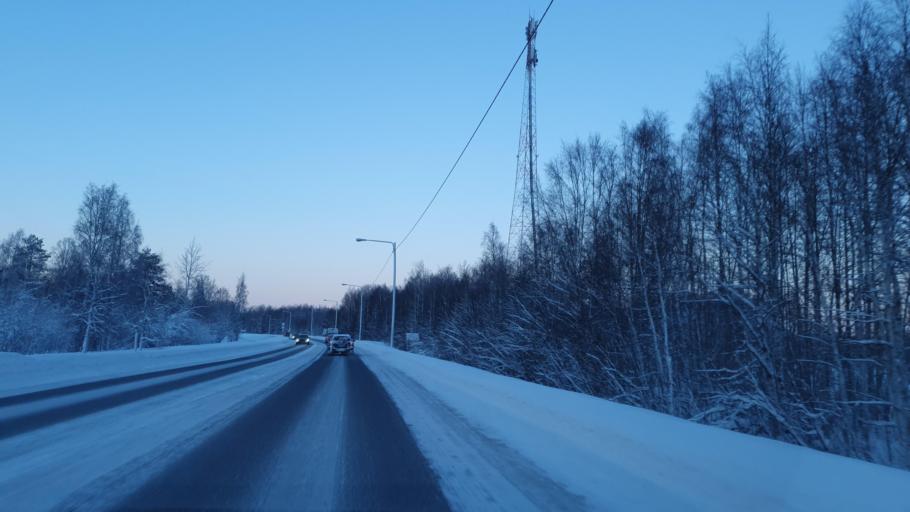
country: FI
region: Lapland
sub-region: Kemi-Tornio
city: Tornio
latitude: 65.8689
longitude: 24.1678
